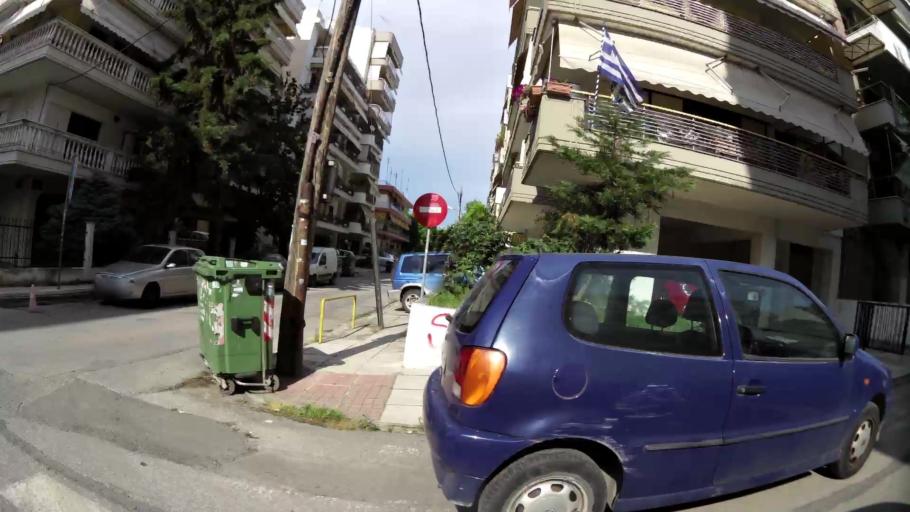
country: GR
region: Central Macedonia
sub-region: Nomos Thessalonikis
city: Kalamaria
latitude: 40.5801
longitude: 22.9578
